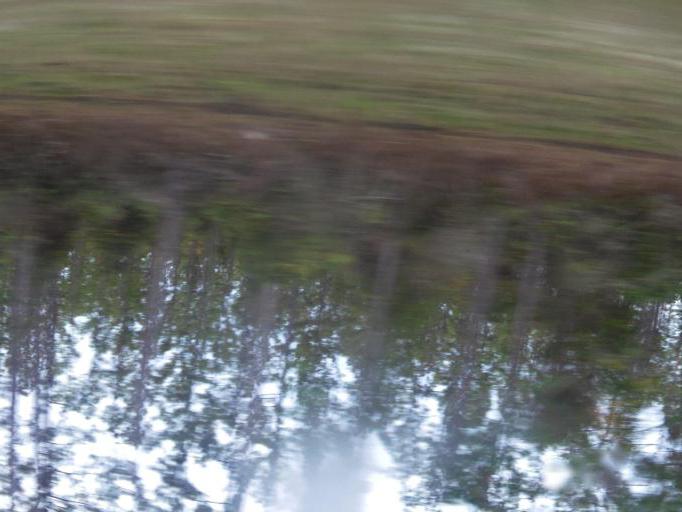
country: US
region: Georgia
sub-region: Charlton County
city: Folkston
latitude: 30.7911
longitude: -82.0408
